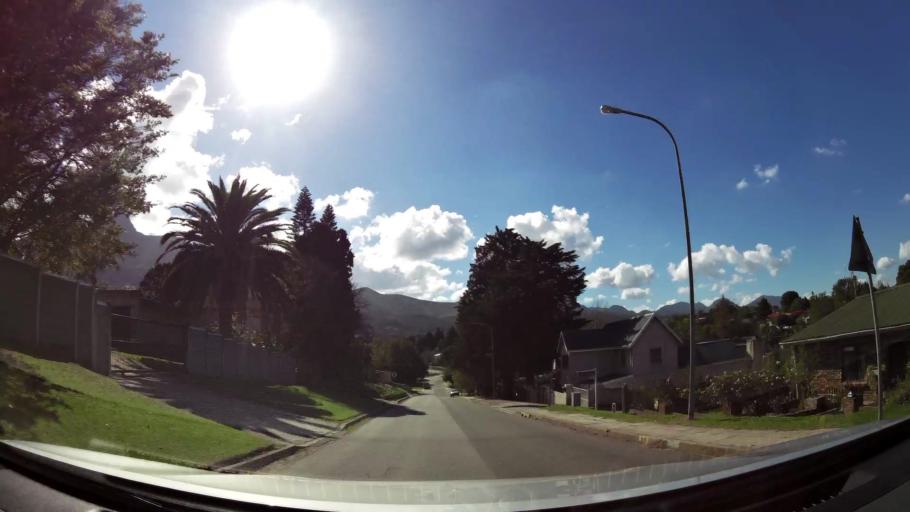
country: ZA
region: Western Cape
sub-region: Eden District Municipality
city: George
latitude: -33.9475
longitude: 22.4681
